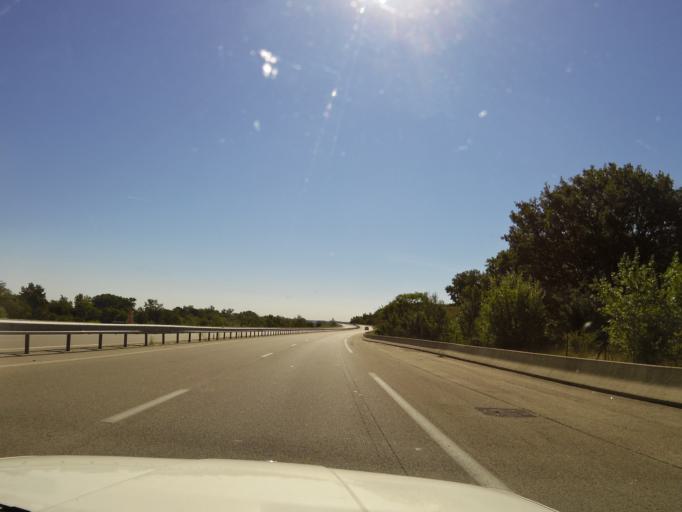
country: FR
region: Languedoc-Roussillon
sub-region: Departement du Gard
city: Moussac
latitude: 43.9716
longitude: 4.2108
